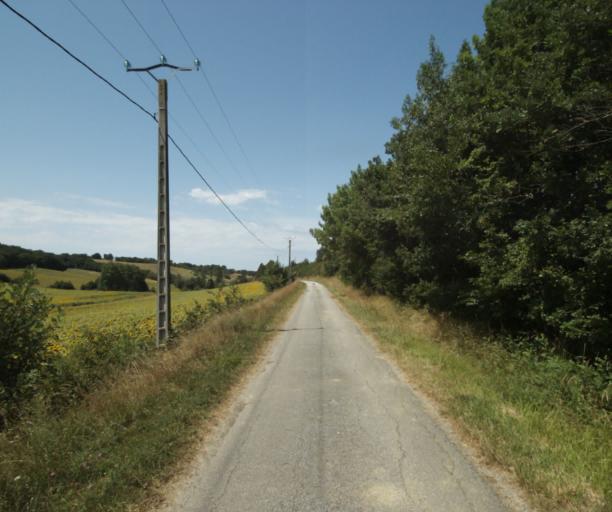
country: FR
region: Midi-Pyrenees
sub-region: Departement de la Haute-Garonne
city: Saint-Felix-Lauragais
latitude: 43.4498
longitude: 1.8649
